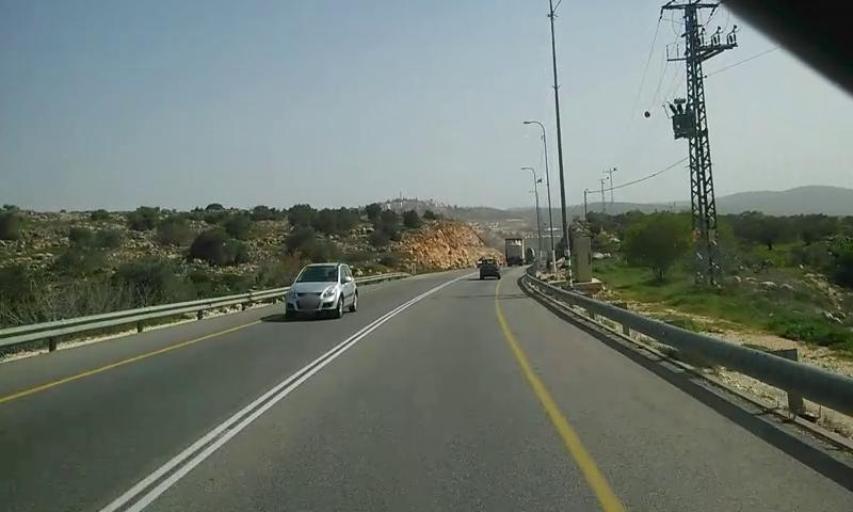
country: PS
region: West Bank
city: Turmus`ayya
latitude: 32.0459
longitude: 35.2889
